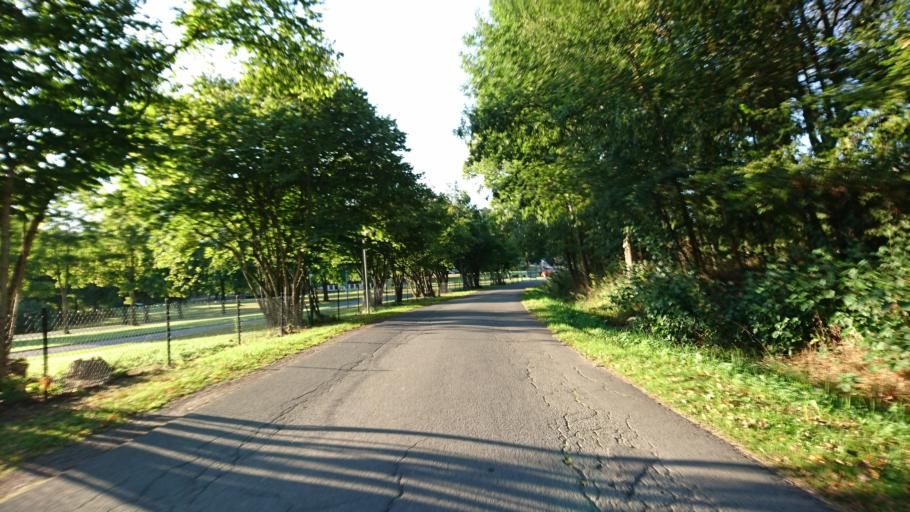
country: SE
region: Joenkoeping
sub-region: Jonkopings Kommun
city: Jonkoping
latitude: 57.8162
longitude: 14.1514
